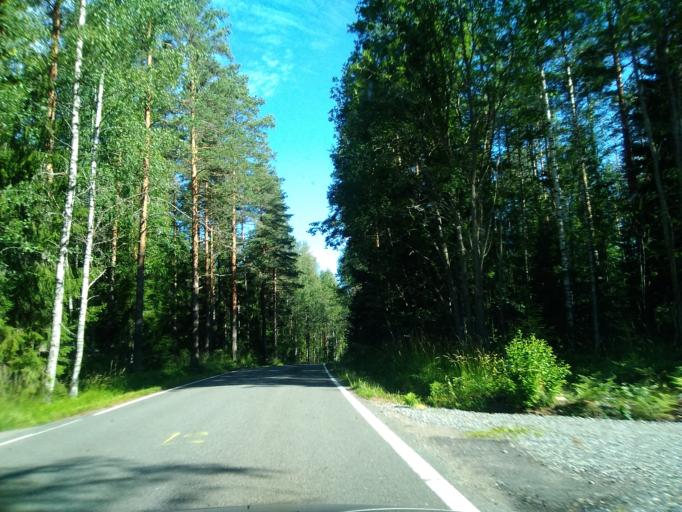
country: FI
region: Uusimaa
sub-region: Helsinki
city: Kaerkoelae
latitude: 60.7918
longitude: 24.0842
